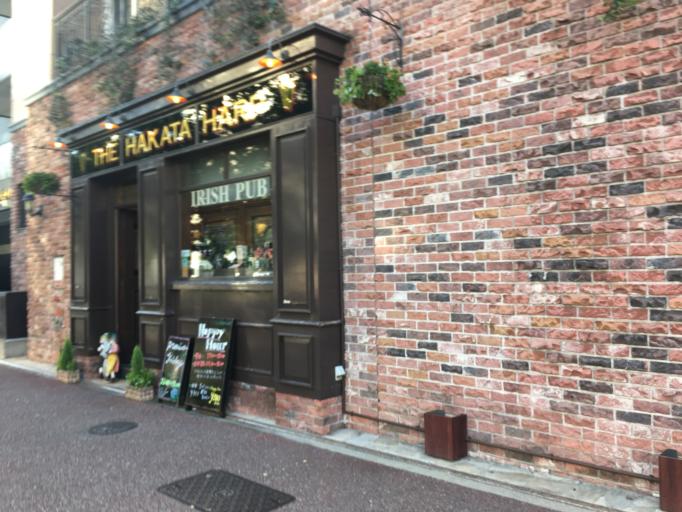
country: JP
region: Fukuoka
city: Fukuoka-shi
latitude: 33.5963
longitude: 130.4048
